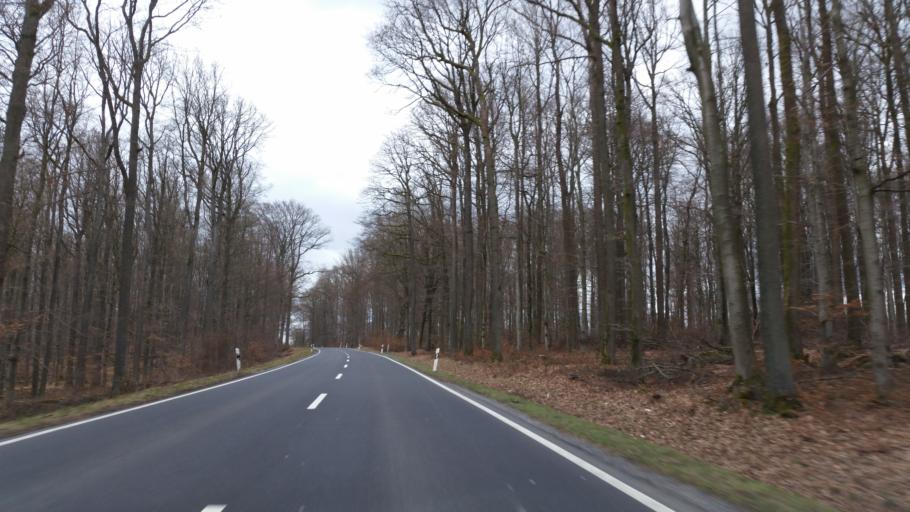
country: DE
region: Bavaria
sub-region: Regierungsbezirk Unterfranken
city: Weibersbrunn
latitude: 49.9456
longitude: 9.3491
